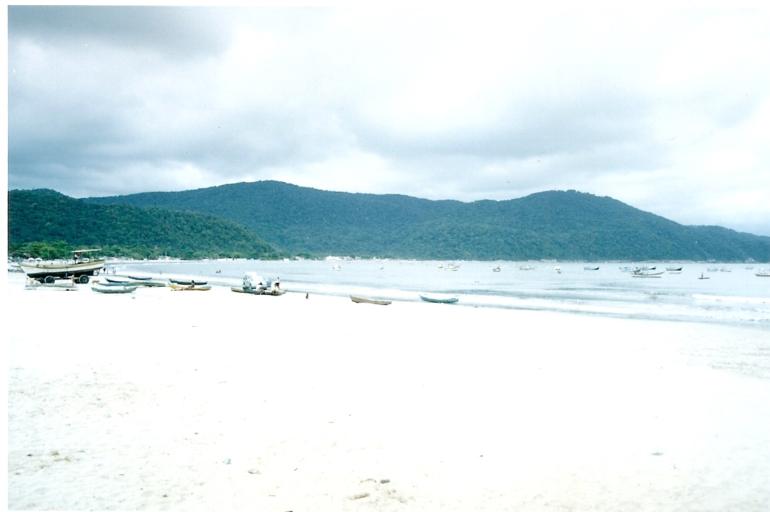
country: BR
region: Sao Paulo
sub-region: Bertioga
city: Bertioga
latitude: -23.9389
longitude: -46.1793
